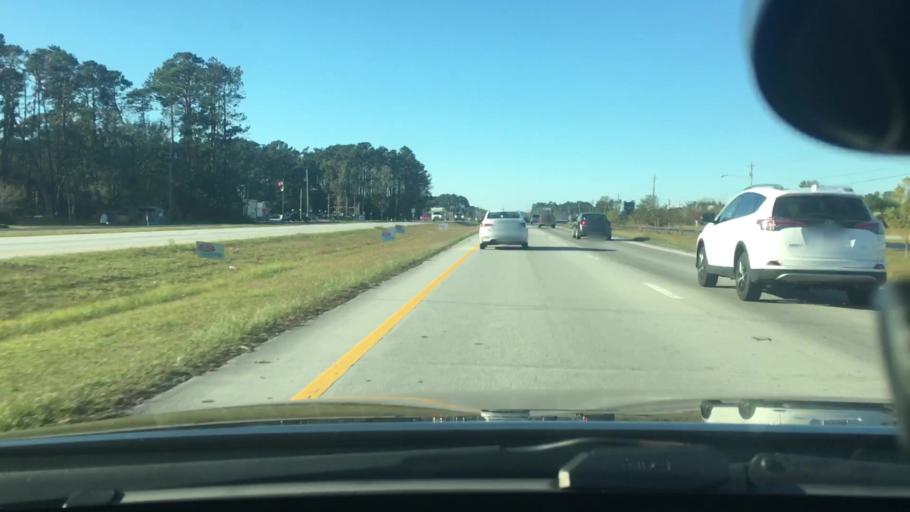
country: US
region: North Carolina
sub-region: Craven County
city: Havelock
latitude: 34.9034
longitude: -76.9322
